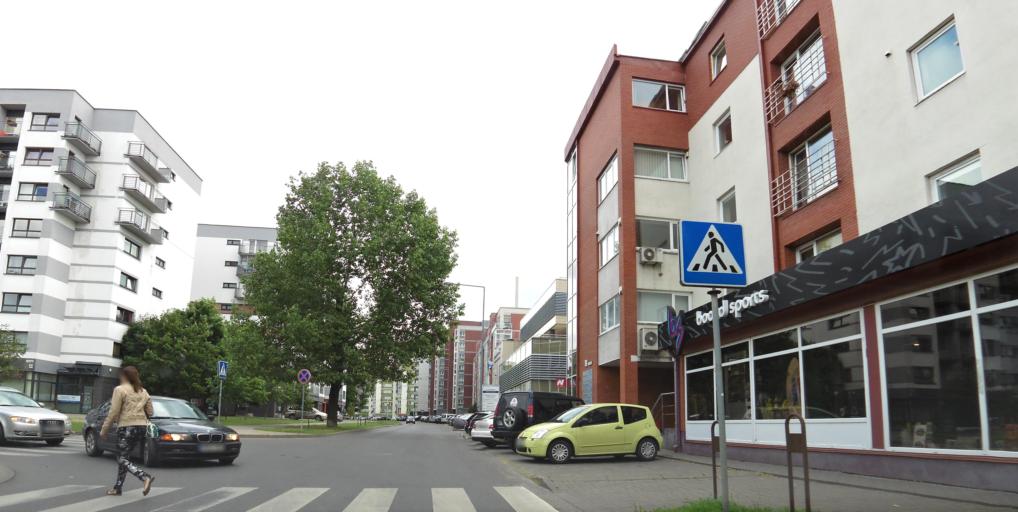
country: LT
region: Vilnius County
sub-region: Vilnius
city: Vilnius
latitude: 54.7075
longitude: 25.2965
